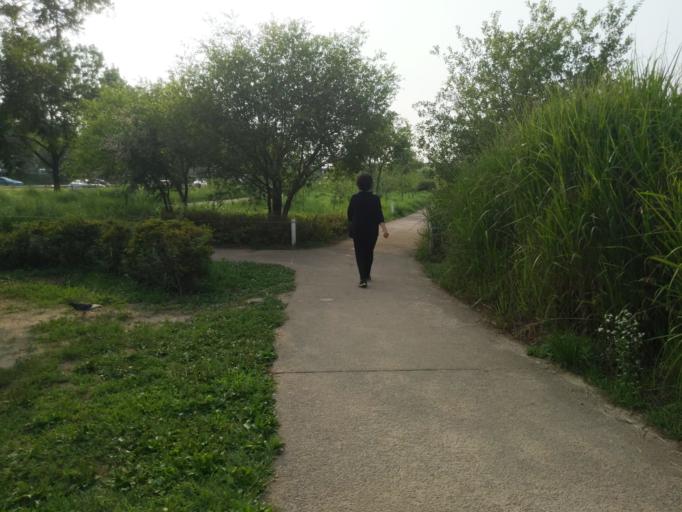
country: KR
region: Gyeonggi-do
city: Kwangmyong
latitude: 37.5377
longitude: 126.9041
